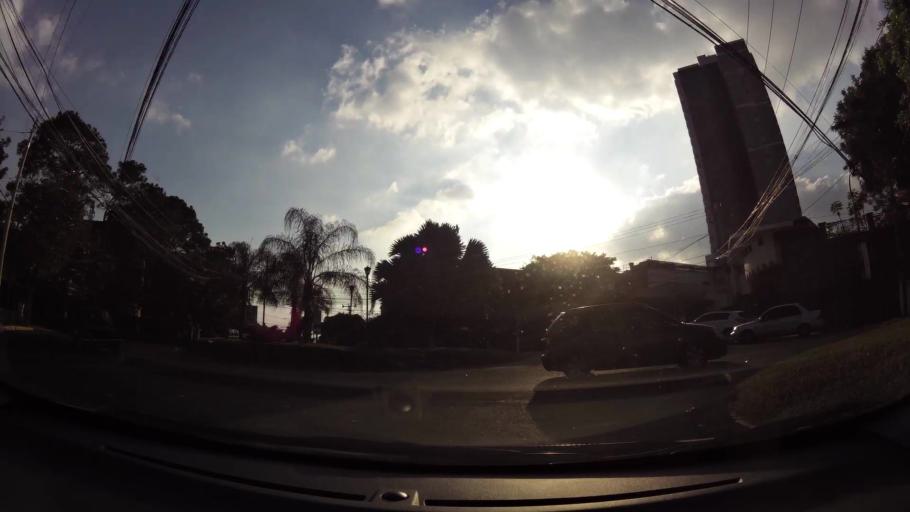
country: SV
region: La Libertad
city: Antiguo Cuscatlan
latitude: 13.6950
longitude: -89.2356
